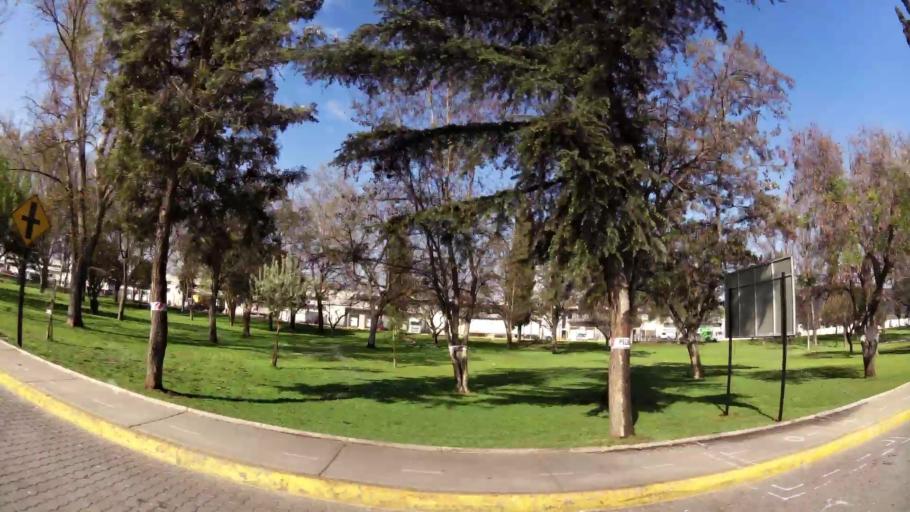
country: CL
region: Santiago Metropolitan
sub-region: Provincia de Santiago
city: Lo Prado
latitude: -33.4067
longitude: -70.7917
